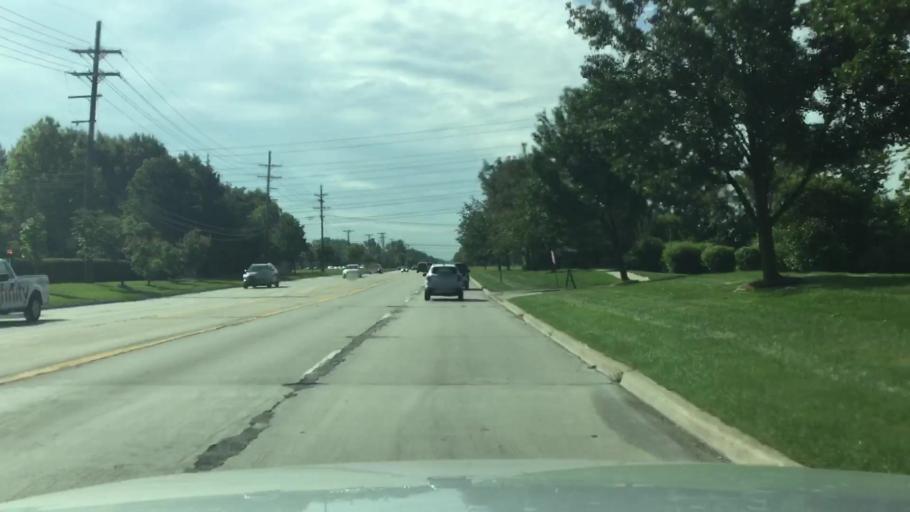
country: US
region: Michigan
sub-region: Wayne County
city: Canton
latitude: 42.3130
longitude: -83.4876
